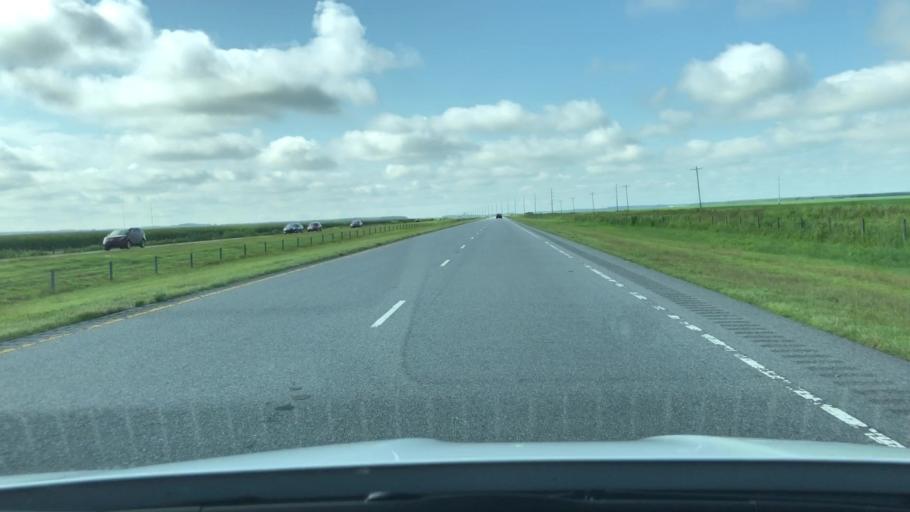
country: US
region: North Carolina
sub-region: Pasquotank County
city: Elizabeth City
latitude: 36.3399
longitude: -76.3131
